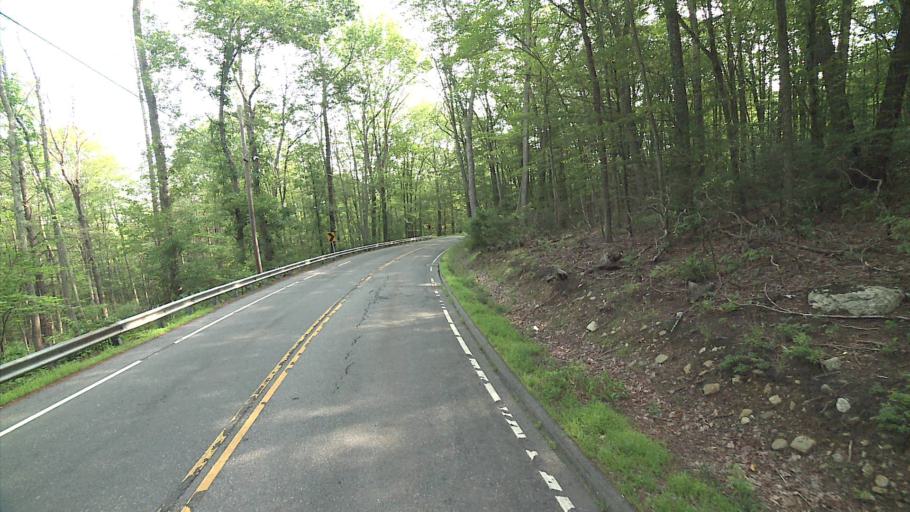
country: US
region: Connecticut
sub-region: Windham County
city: Quinebaug
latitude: 41.9919
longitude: -72.0160
